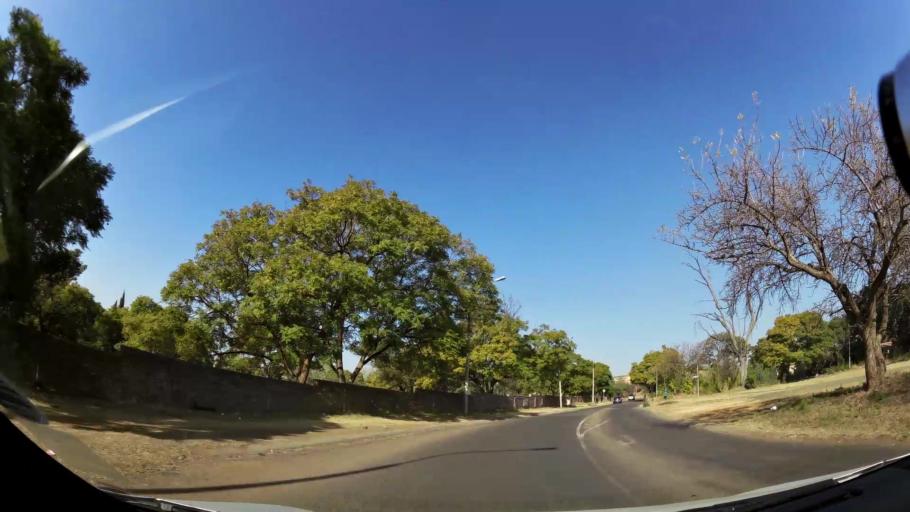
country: ZA
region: North-West
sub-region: Bojanala Platinum District Municipality
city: Rustenburg
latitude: -25.6751
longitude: 27.2436
